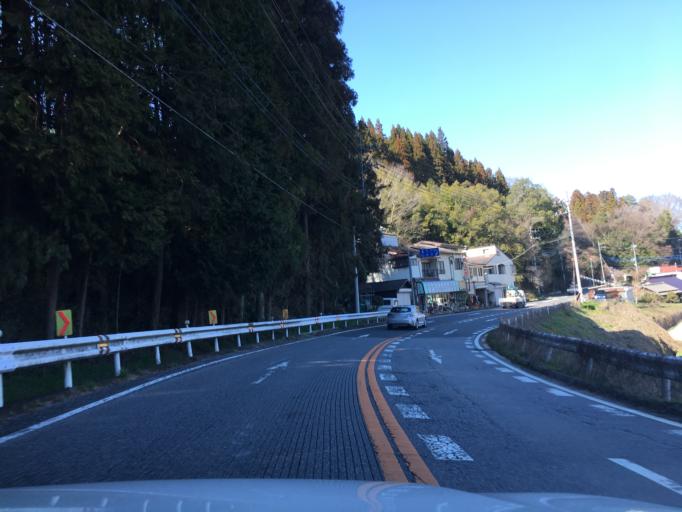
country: JP
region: Tochigi
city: Motegi
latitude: 36.5571
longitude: 140.2381
